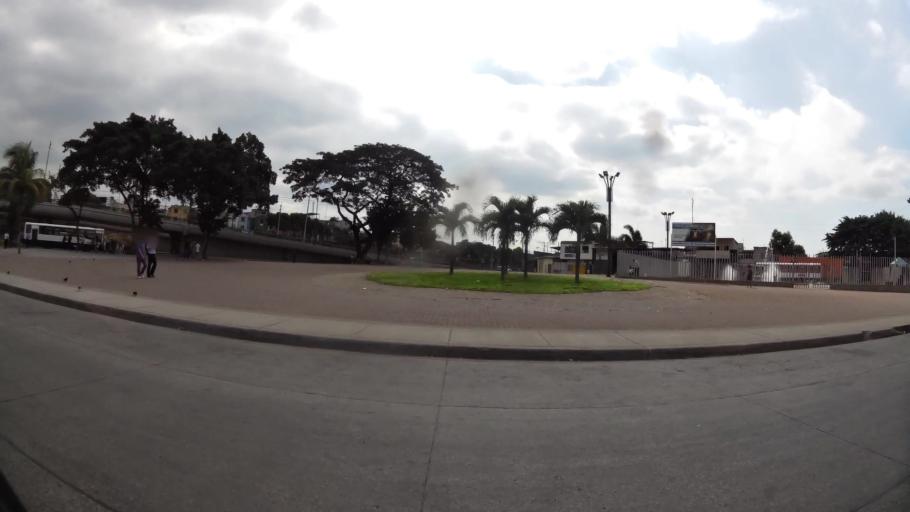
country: EC
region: Guayas
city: Santa Lucia
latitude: -2.0907
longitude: -79.9362
